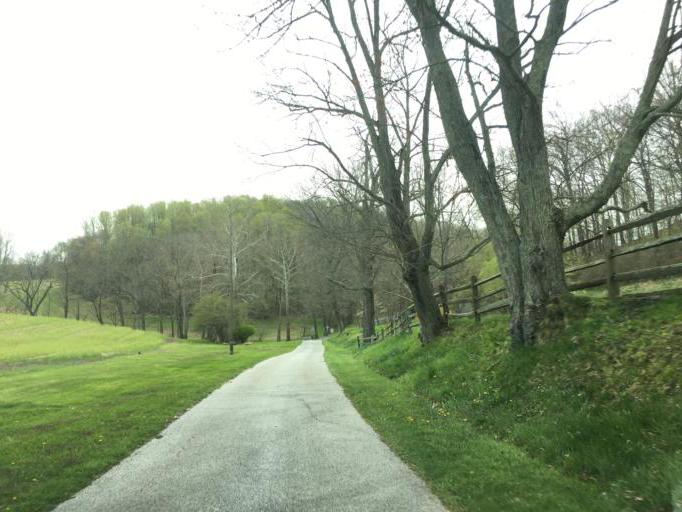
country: US
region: Maryland
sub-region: Baltimore County
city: Hunt Valley
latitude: 39.5628
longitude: -76.6467
